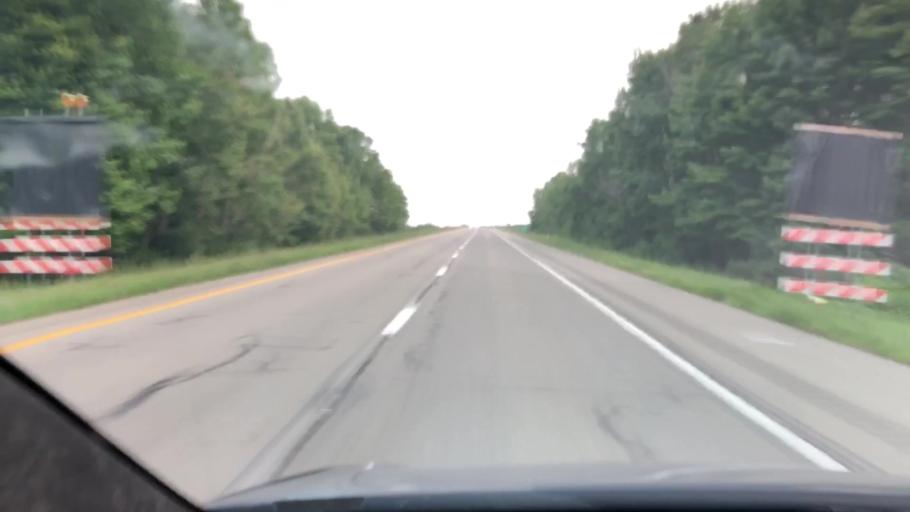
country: US
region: Pennsylvania
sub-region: Venango County
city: Franklin
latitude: 41.2744
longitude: -79.9181
